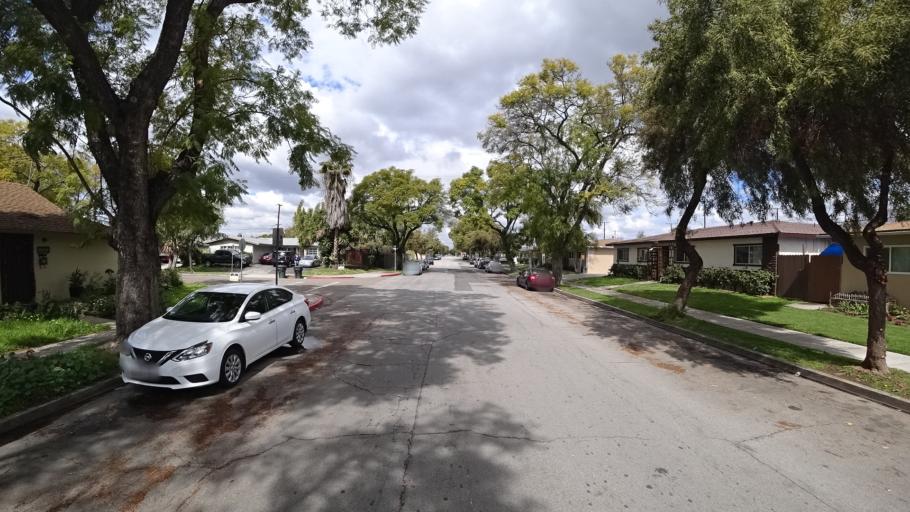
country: US
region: California
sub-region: Orange County
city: Anaheim
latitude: 33.8186
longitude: -117.9334
